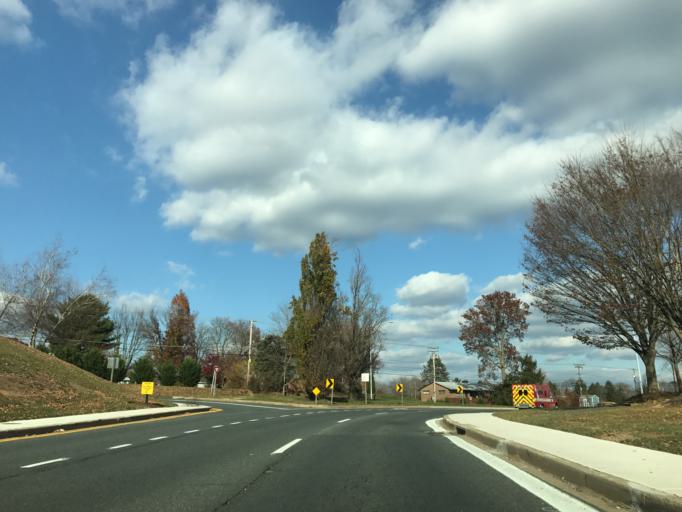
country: US
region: Maryland
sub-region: Harford County
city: South Bel Air
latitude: 39.5368
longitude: -76.3423
